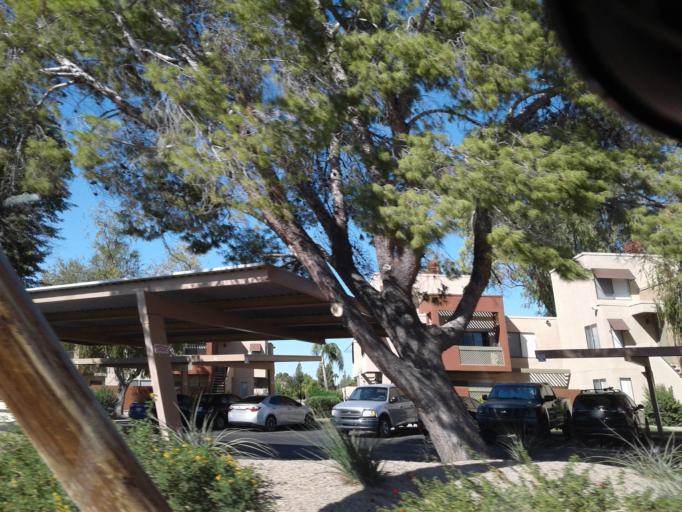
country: US
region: Arizona
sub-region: Maricopa County
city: Scottsdale
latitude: 33.4930
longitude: -111.9090
